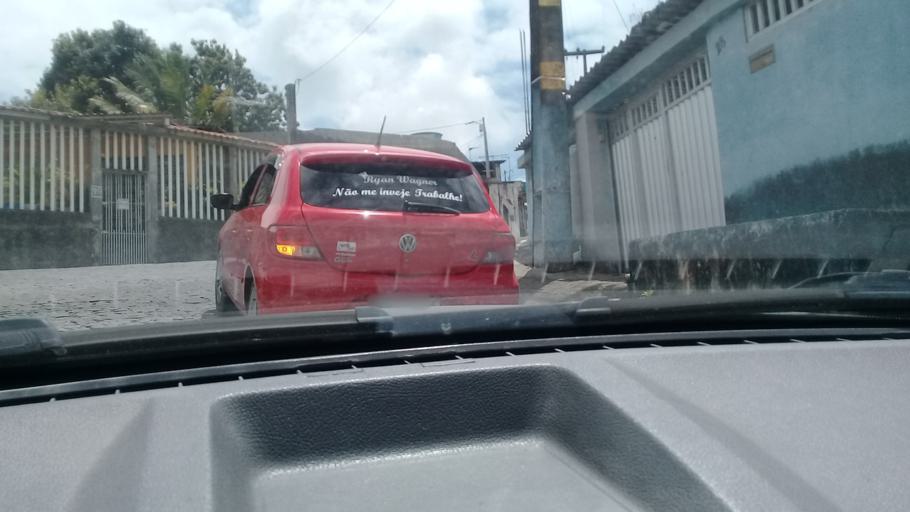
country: BR
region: Pernambuco
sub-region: Jaboatao Dos Guararapes
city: Jaboatao dos Guararapes
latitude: -8.1209
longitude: -34.9491
